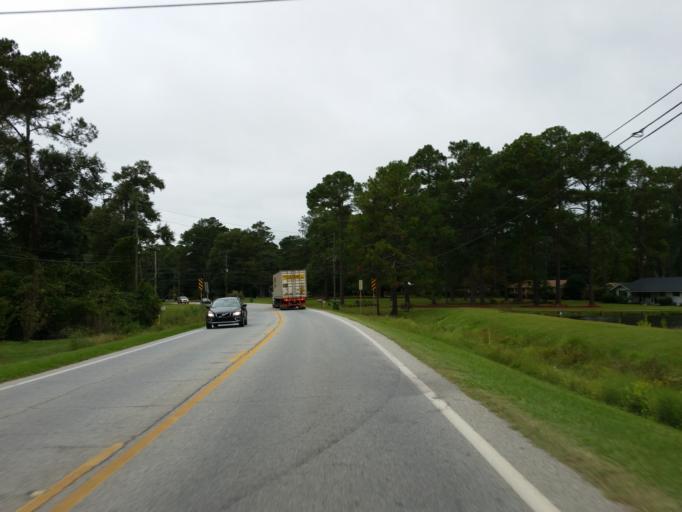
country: US
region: Georgia
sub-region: Cook County
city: Adel
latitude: 31.1394
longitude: -83.4123
